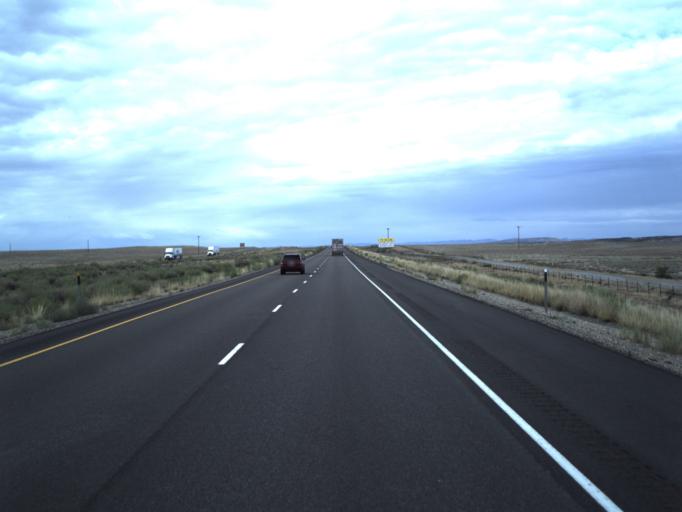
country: US
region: Colorado
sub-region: Mesa County
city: Loma
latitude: 39.0470
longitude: -109.2707
